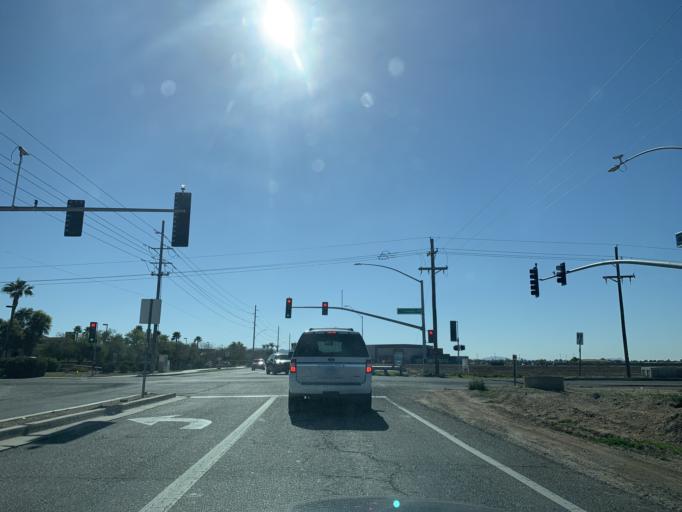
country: US
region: Arizona
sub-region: Pinal County
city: Casa Grande
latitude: 32.9091
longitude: -111.7226
